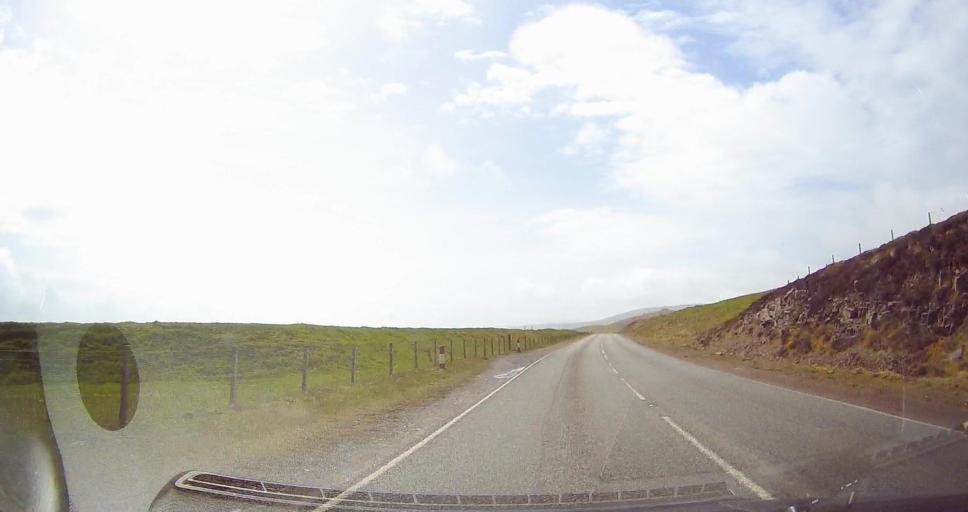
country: GB
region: Scotland
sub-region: Shetland Islands
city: Lerwick
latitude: 60.1199
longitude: -1.2150
